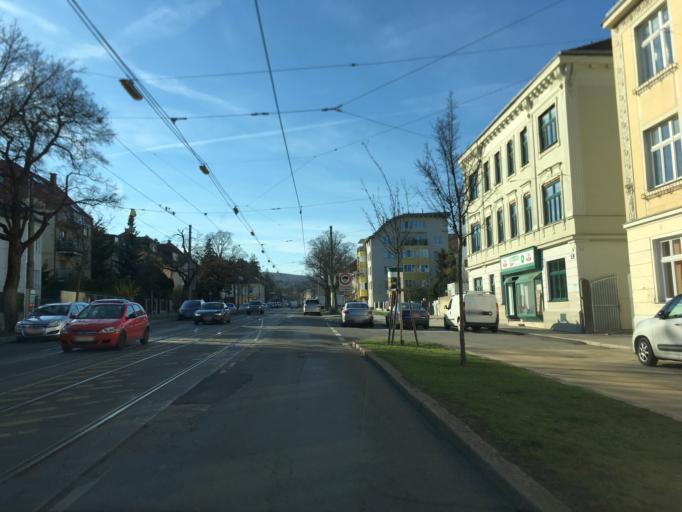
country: AT
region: Vienna
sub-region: Wien Stadt
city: Vienna
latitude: 48.2266
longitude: 16.3072
